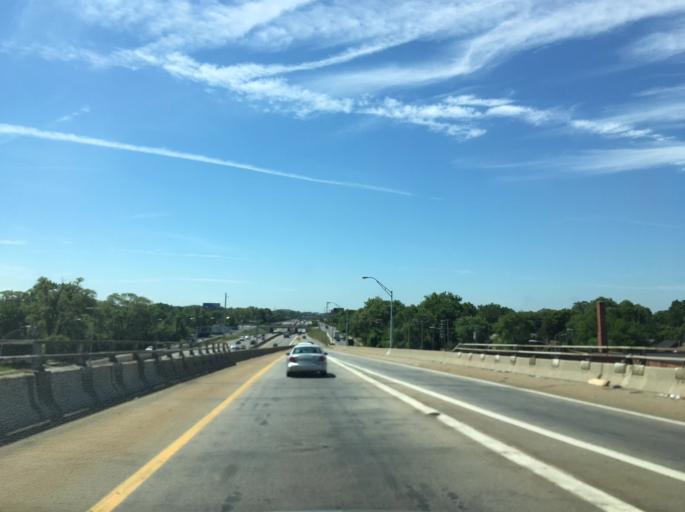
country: US
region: Michigan
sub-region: Wayne County
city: Dearborn
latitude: 42.3773
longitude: -83.2172
